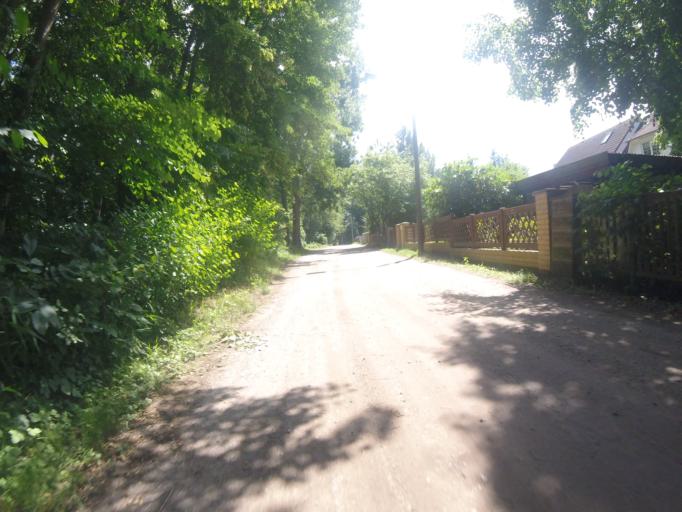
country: DE
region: Brandenburg
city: Bestensee
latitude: 52.2638
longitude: 13.6452
